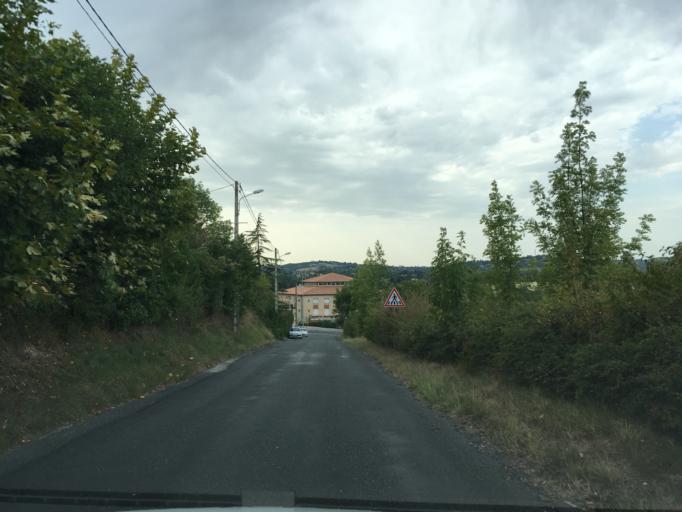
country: FR
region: Midi-Pyrenees
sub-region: Departement du Tarn
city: Castres
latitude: 43.6081
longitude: 2.2597
